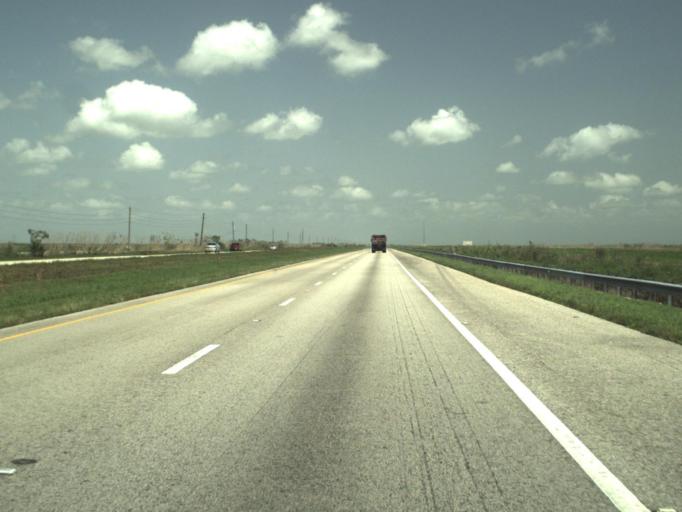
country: US
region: Florida
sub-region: Palm Beach County
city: Belle Glade Camp
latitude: 26.4060
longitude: -80.5926
